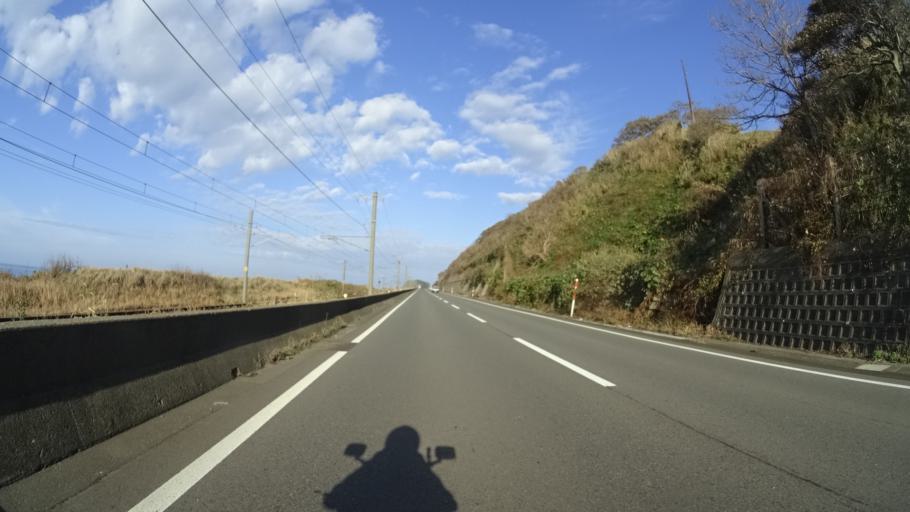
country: JP
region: Niigata
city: Kashiwazaki
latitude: 37.3031
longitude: 138.4153
